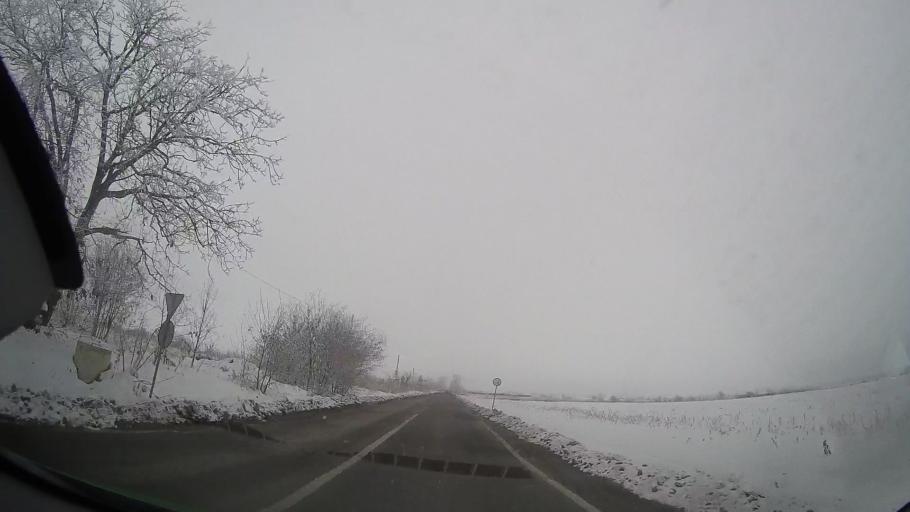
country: RO
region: Neamt
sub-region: Comuna Horia
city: Cotu Vames
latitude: 46.9387
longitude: 26.9490
